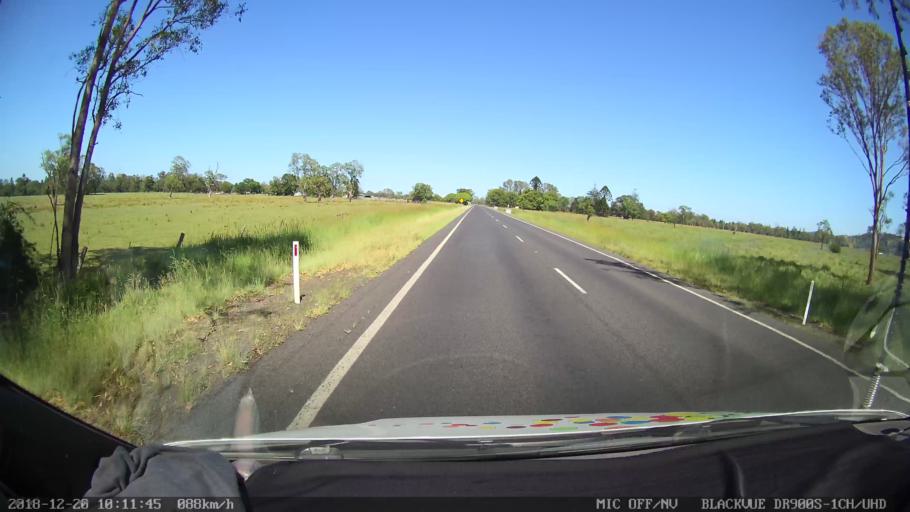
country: AU
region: New South Wales
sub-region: Richmond Valley
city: Casino
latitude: -28.8724
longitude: 153.1543
